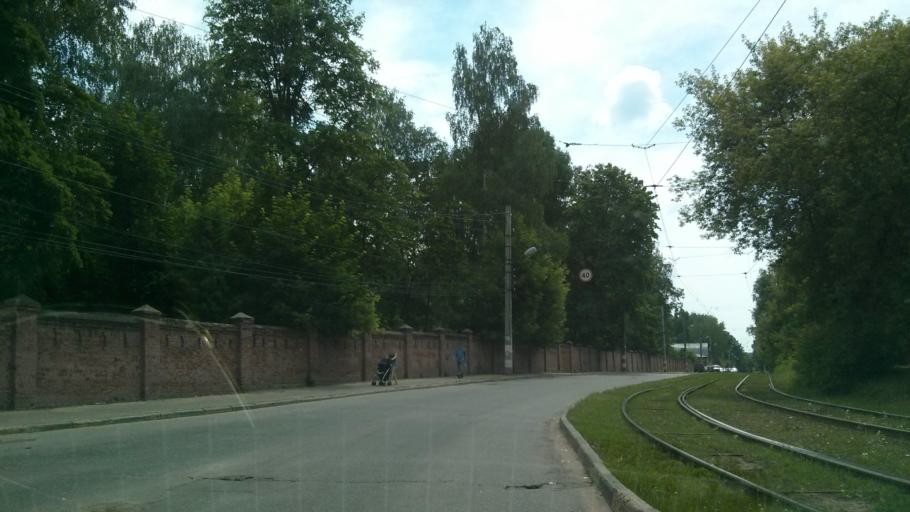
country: RU
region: Nizjnij Novgorod
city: Nizhniy Novgorod
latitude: 56.3019
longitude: 43.9911
